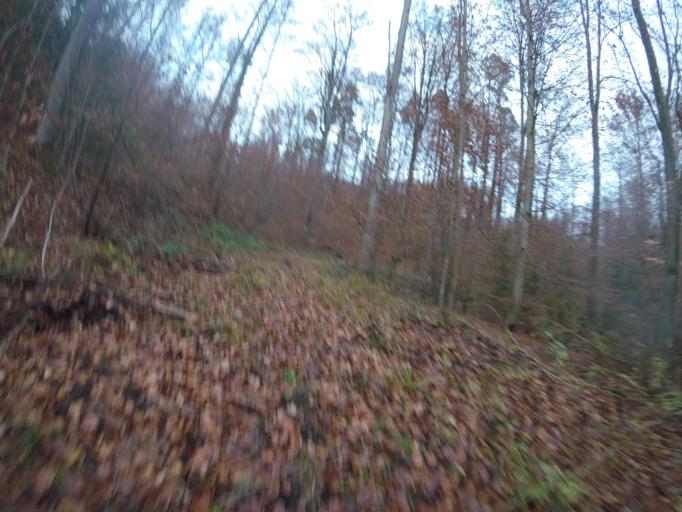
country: DE
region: Baden-Wuerttemberg
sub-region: Regierungsbezirk Stuttgart
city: Aspach
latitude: 49.0066
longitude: 9.3976
